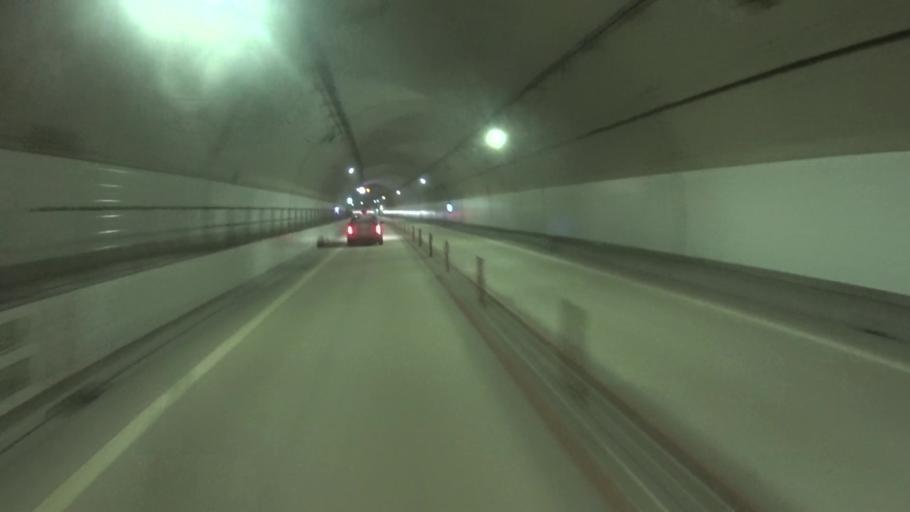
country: JP
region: Kyoto
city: Miyazu
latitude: 35.5293
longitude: 135.1725
